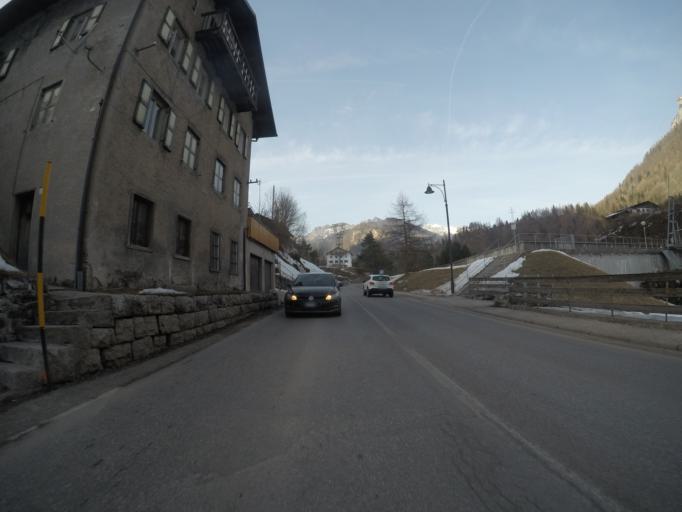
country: IT
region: Veneto
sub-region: Provincia di Belluno
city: Cencenighe Agordino
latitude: 46.3436
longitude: 11.9728
